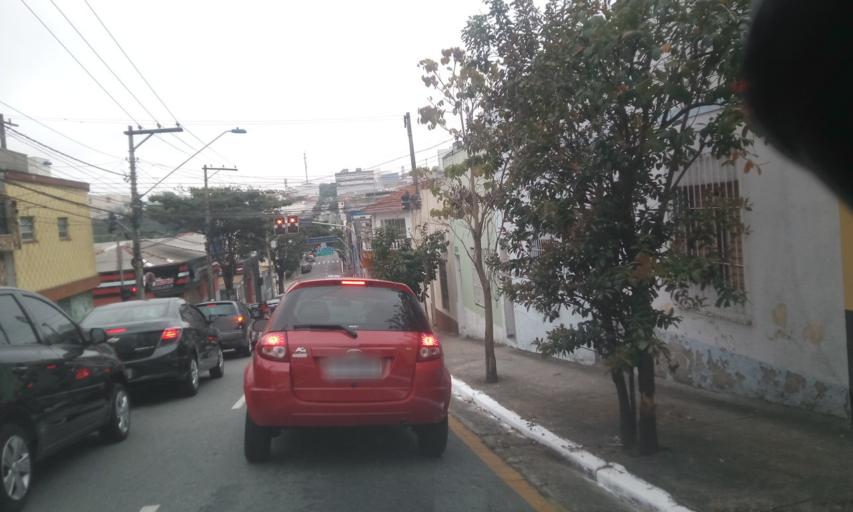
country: BR
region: Sao Paulo
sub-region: Sao Caetano Do Sul
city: Sao Caetano do Sul
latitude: -23.6335
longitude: -46.5692
